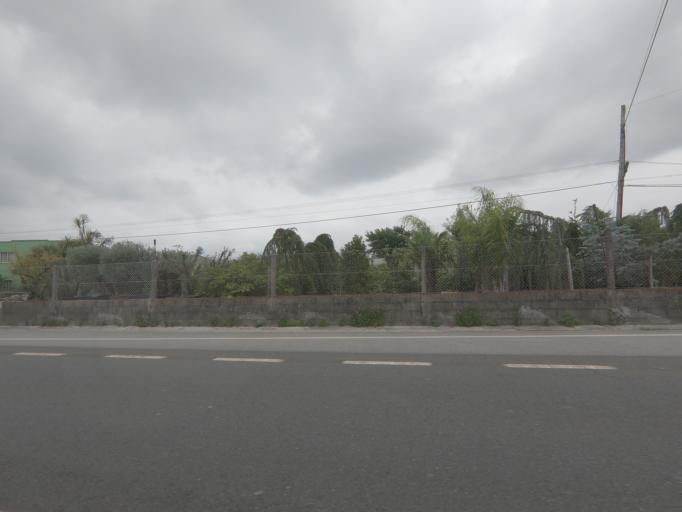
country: PT
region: Viana do Castelo
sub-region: Vila Nova de Cerveira
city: Vila Nova de Cerveira
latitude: 41.9598
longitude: -8.7634
